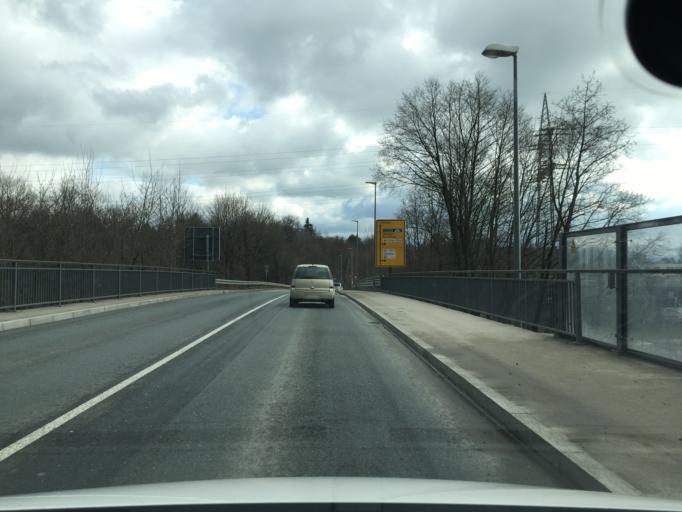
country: DE
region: Bavaria
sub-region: Upper Bavaria
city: Rosenheim
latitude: 47.8471
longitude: 12.1372
